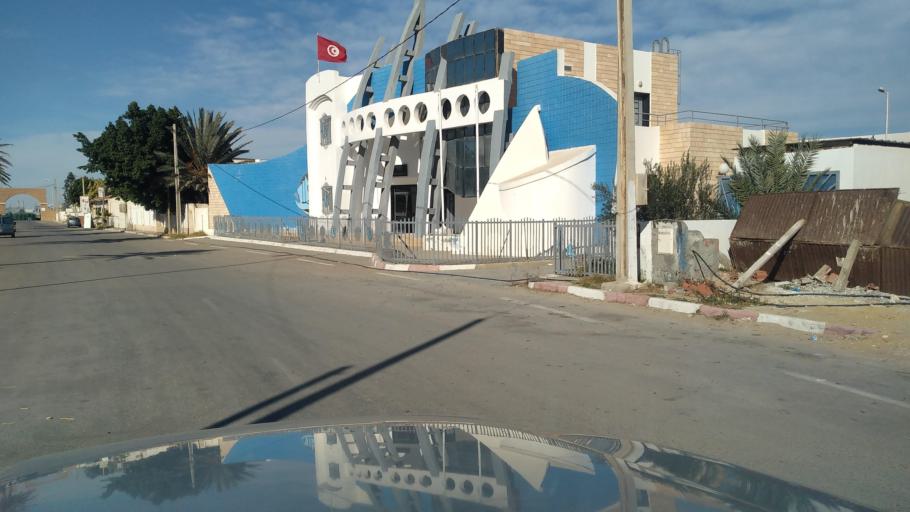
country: TN
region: Qabis
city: Gabes
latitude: 33.8928
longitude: 10.1152
